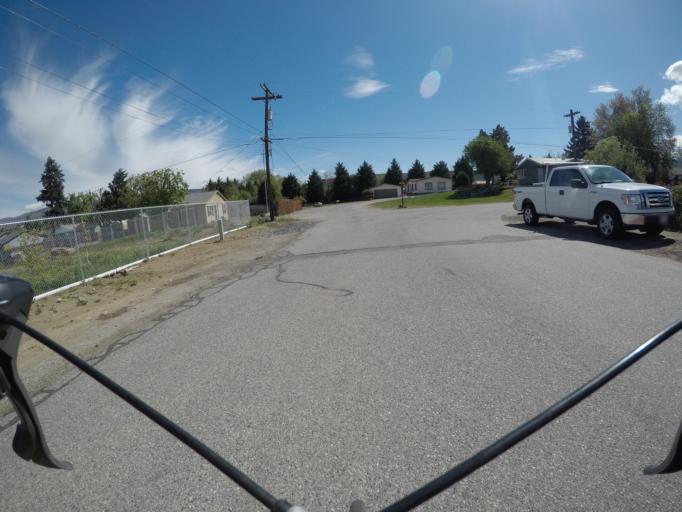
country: US
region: Washington
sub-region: Chelan County
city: South Wenatchee
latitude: 47.4028
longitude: -120.2857
